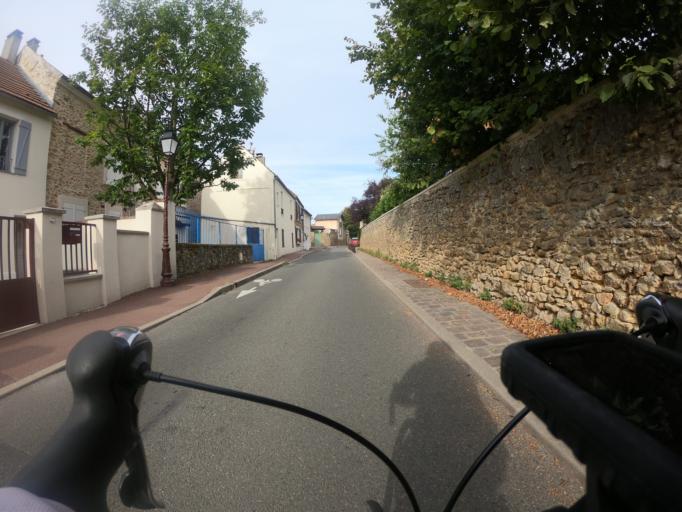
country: FR
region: Ile-de-France
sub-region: Departement des Yvelines
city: Les Loges-en-Josas
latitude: 48.7645
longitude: 2.1436
